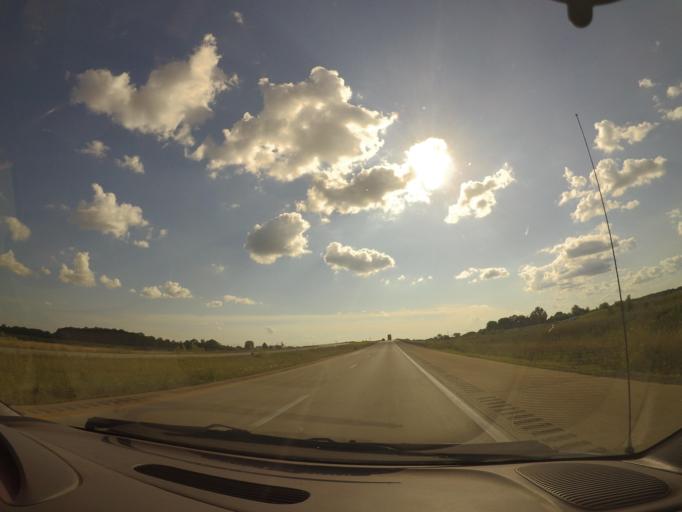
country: US
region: Ohio
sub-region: Lucas County
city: Waterville
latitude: 41.5252
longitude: -83.7281
